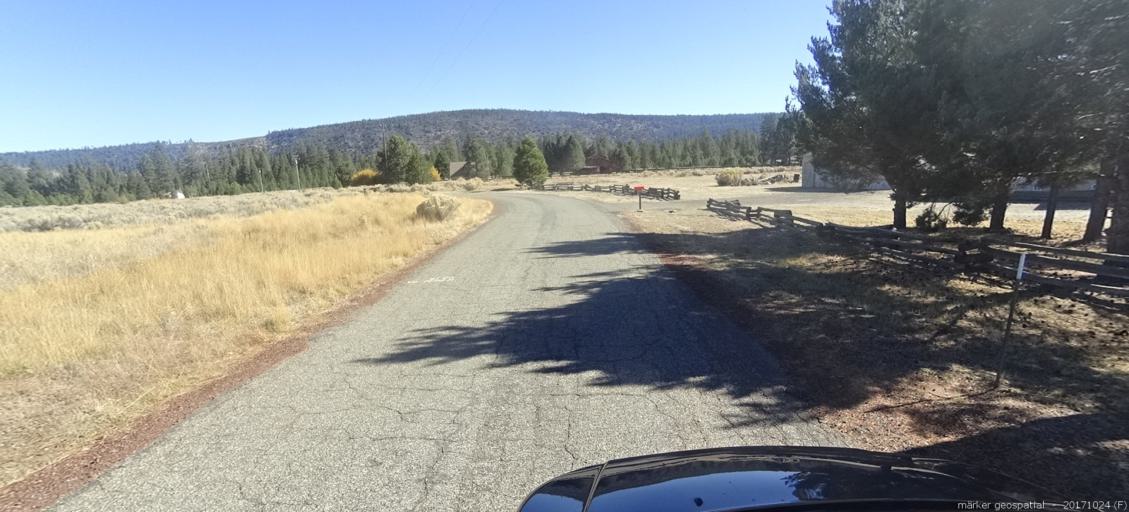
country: US
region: California
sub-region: Shasta County
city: Burney
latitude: 40.6736
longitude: -121.4305
